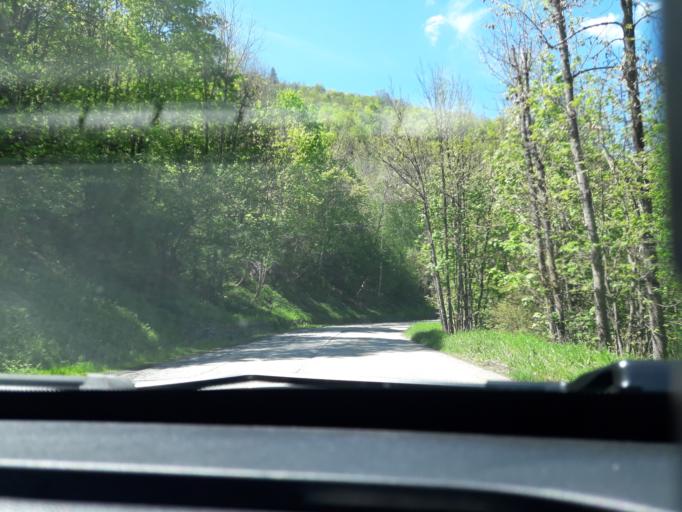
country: FR
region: Rhone-Alpes
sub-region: Departement de la Savoie
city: Saint-Martin-de-Belleville
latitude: 45.4116
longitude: 6.4884
